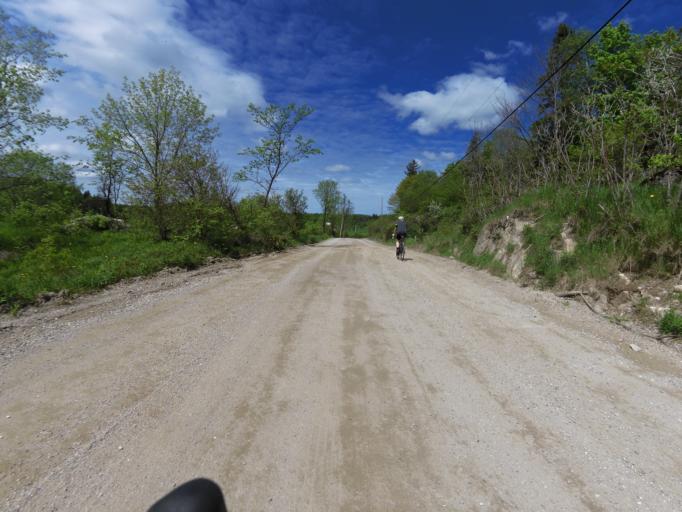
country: CA
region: Quebec
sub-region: Outaouais
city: Wakefield
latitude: 45.7837
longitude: -76.0032
